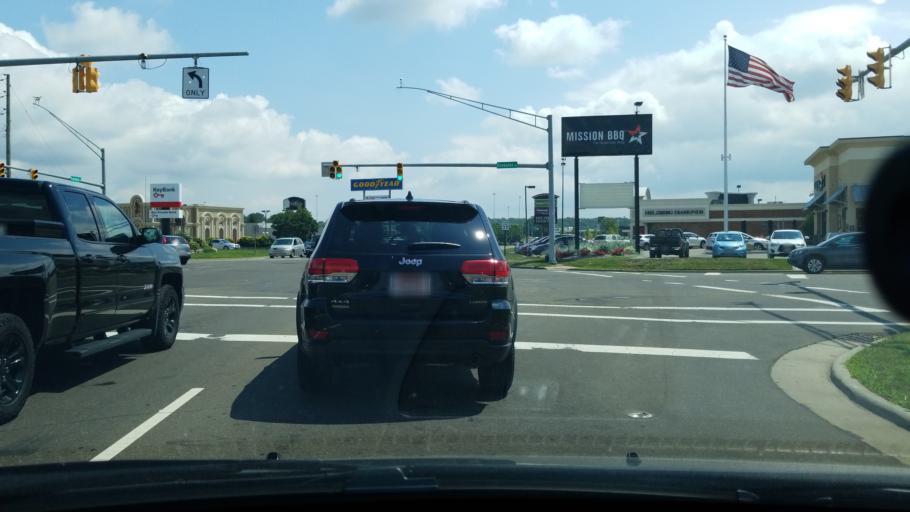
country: US
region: Ohio
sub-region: Stark County
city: North Canton
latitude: 40.8585
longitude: -81.4329
